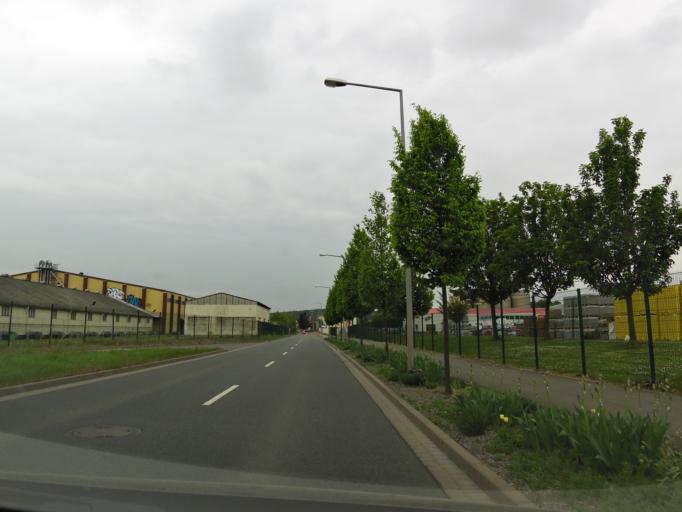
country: DE
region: Thuringia
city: Gotha
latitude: 50.9507
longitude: 10.7273
